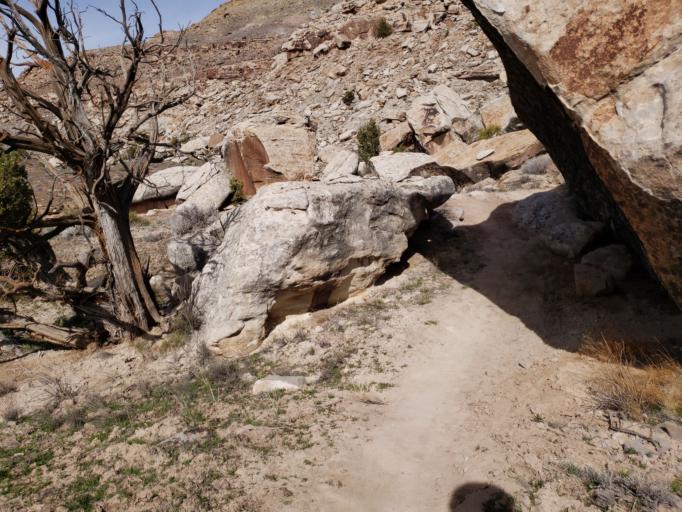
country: US
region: Colorado
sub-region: Mesa County
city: Loma
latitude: 39.1932
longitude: -108.8815
